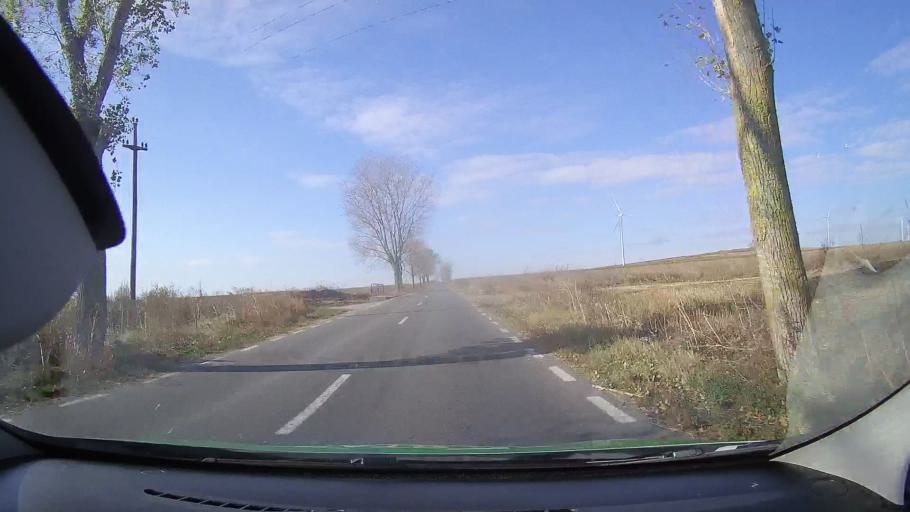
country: RO
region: Tulcea
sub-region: Comuna Valea Nucarilor
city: Iazurile
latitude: 45.0257
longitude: 28.9928
